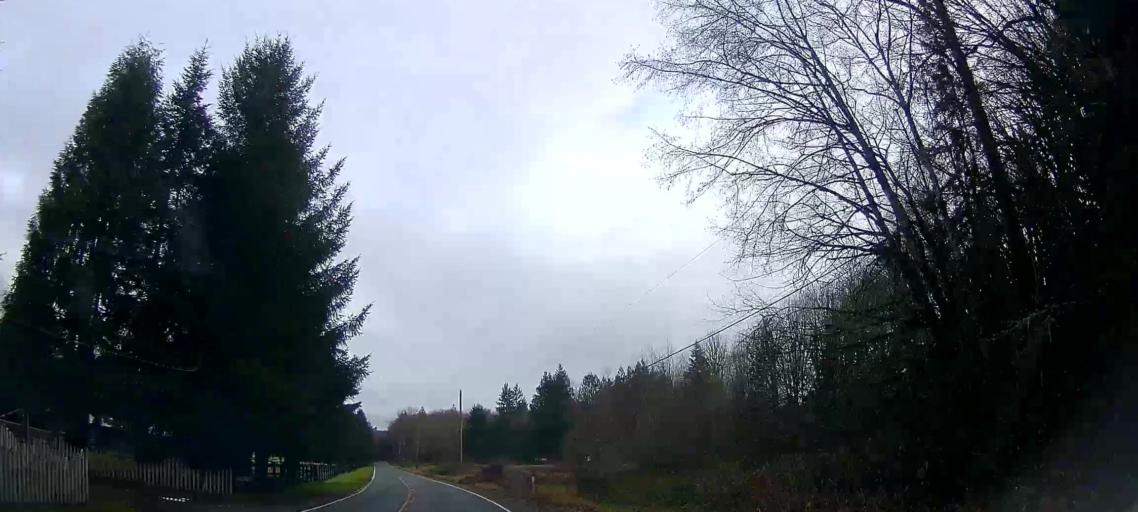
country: US
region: Washington
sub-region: Snohomish County
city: Darrington
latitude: 48.5173
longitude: -121.8485
